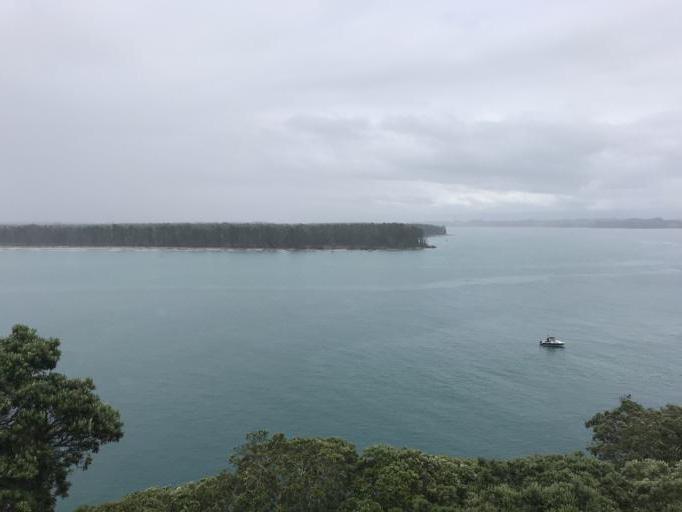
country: NZ
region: Bay of Plenty
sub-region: Western Bay of Plenty District
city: Waihi Beach
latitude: -37.4684
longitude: 175.9866
